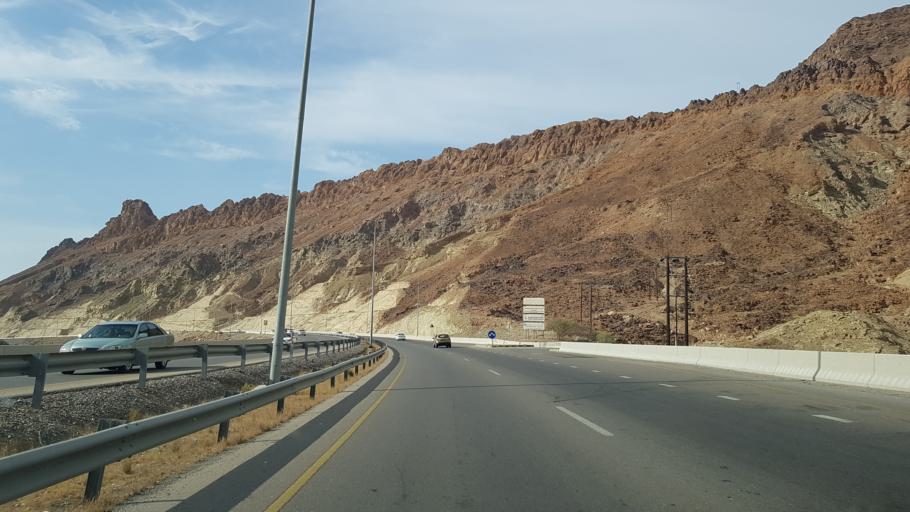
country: OM
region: Muhafazat ad Dakhiliyah
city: Bidbid
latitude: 23.4476
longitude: 58.1232
